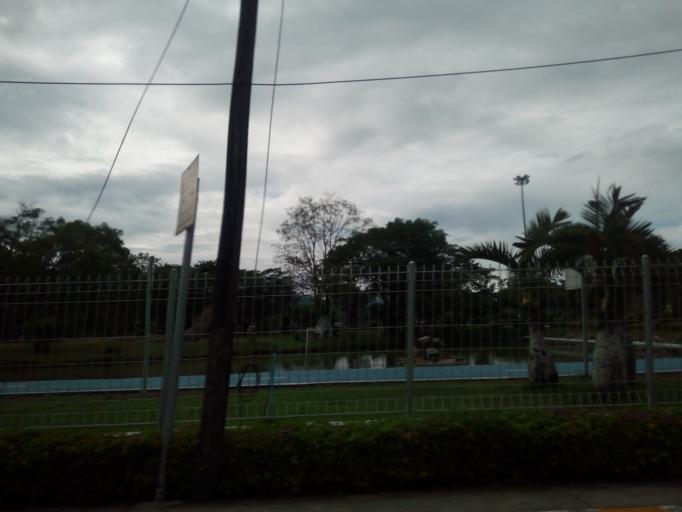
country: TH
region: Phuket
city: Ban Talat Nua
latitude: 7.8740
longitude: 98.3793
